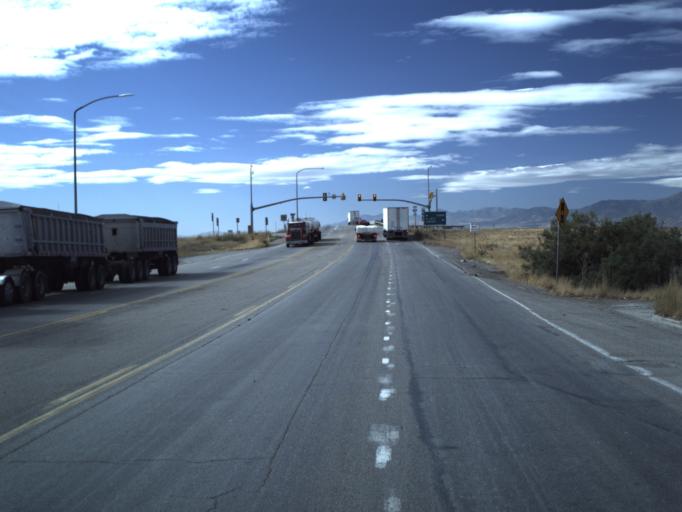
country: US
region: Utah
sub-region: Davis County
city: North Salt Lake
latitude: 40.8363
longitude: -111.9348
